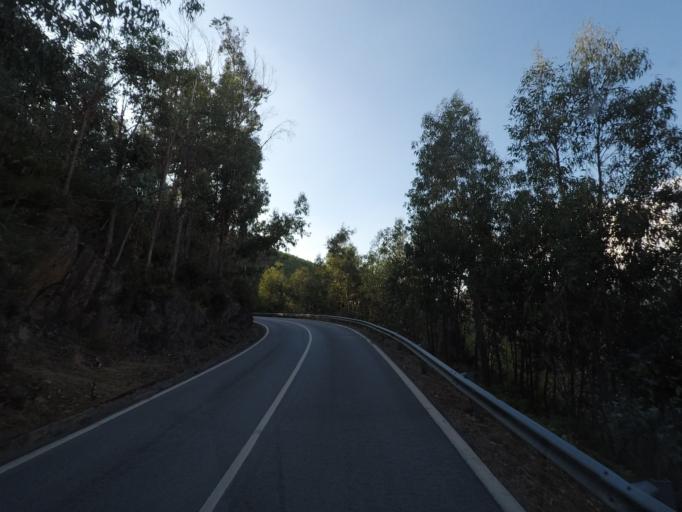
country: PT
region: Vila Real
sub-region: Mesao Frio
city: Mesao Frio
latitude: 41.1758
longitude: -7.9256
